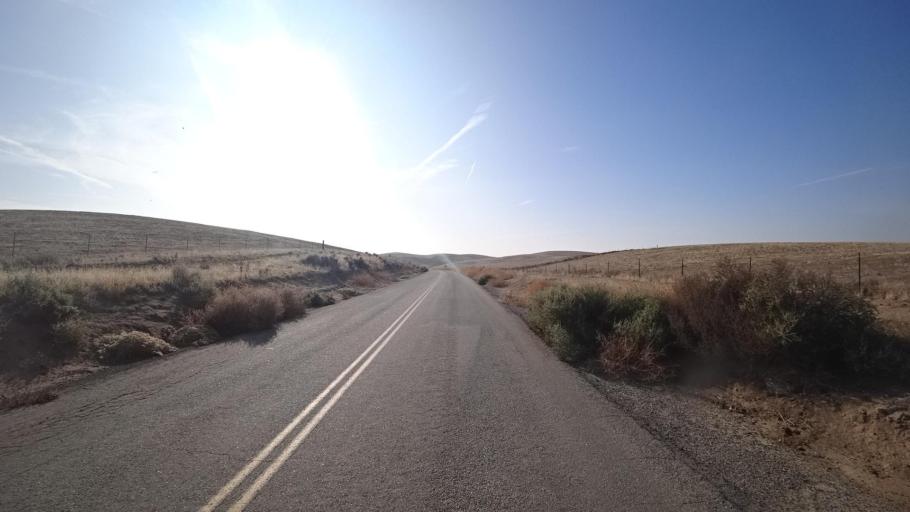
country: US
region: California
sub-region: Tulare County
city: Richgrove
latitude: 35.6254
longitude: -119.0294
